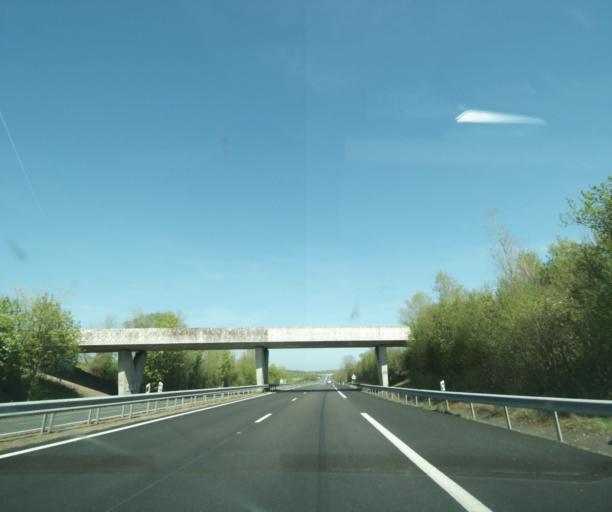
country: FR
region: Bourgogne
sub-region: Departement de la Nievre
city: La Charite-sur-Loire
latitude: 47.1392
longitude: 3.0437
